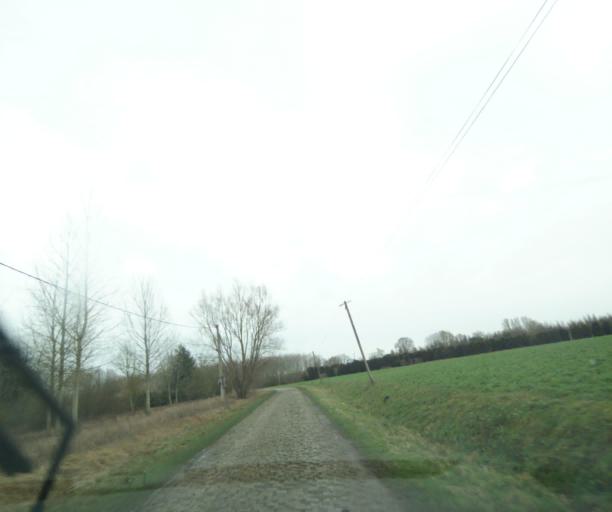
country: FR
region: Nord-Pas-de-Calais
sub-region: Departement du Nord
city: Vicq
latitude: 50.4225
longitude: 3.6154
